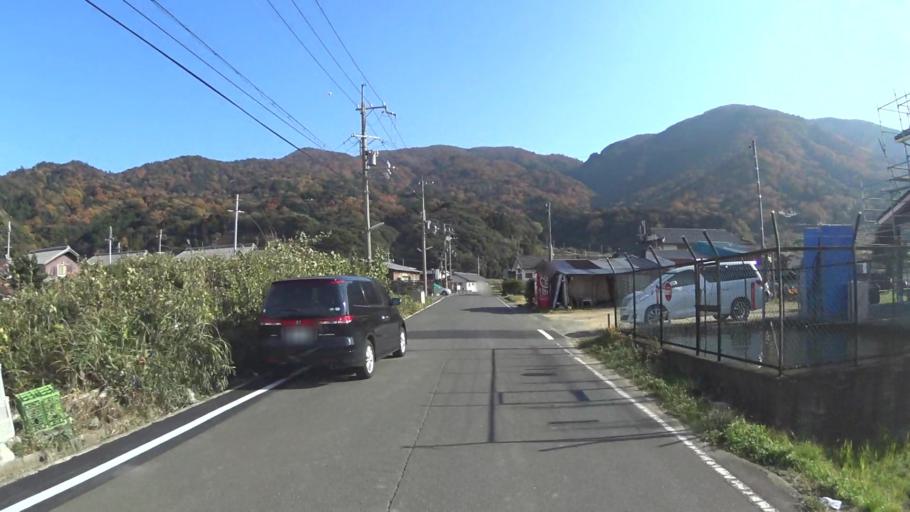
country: JP
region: Kyoto
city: Maizuru
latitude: 35.5596
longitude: 135.4012
